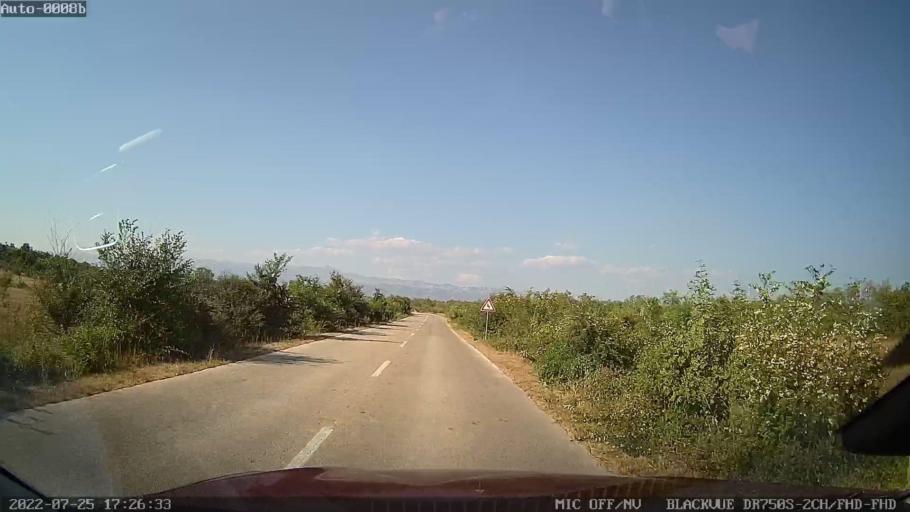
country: HR
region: Zadarska
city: Pridraga
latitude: 44.1346
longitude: 15.5013
